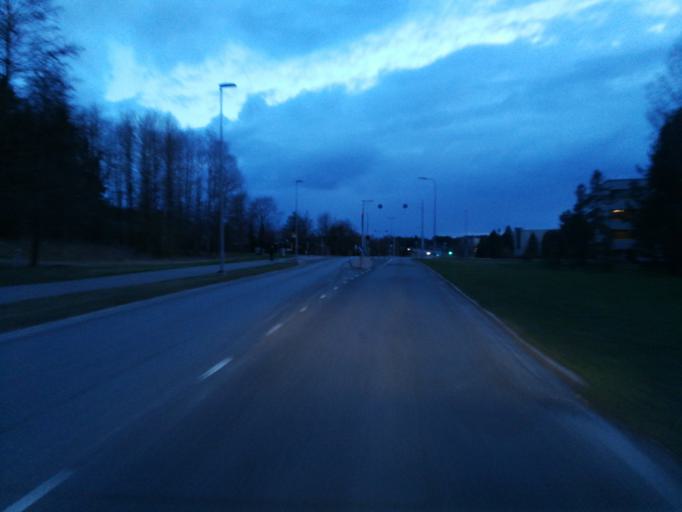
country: FI
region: Varsinais-Suomi
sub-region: Turku
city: Turku
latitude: 60.4656
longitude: 22.2182
